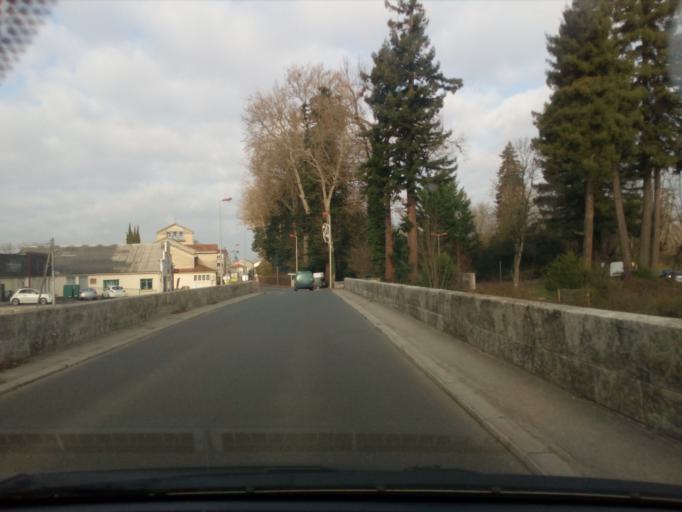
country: FR
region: Poitou-Charentes
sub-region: Departement de la Charente
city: Gond-Pontouvre
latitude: 45.6711
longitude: 0.1603
